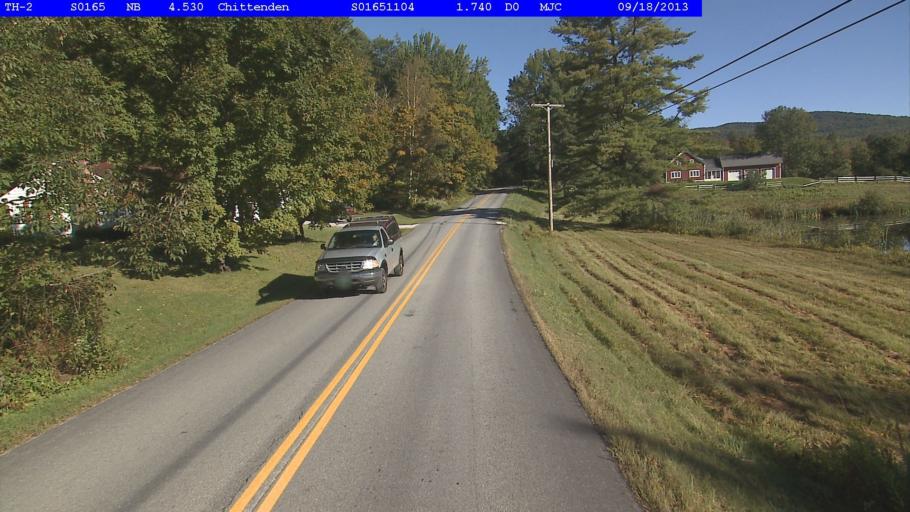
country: US
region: Vermont
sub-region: Rutland County
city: Rutland
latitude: 43.7008
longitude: -72.9595
